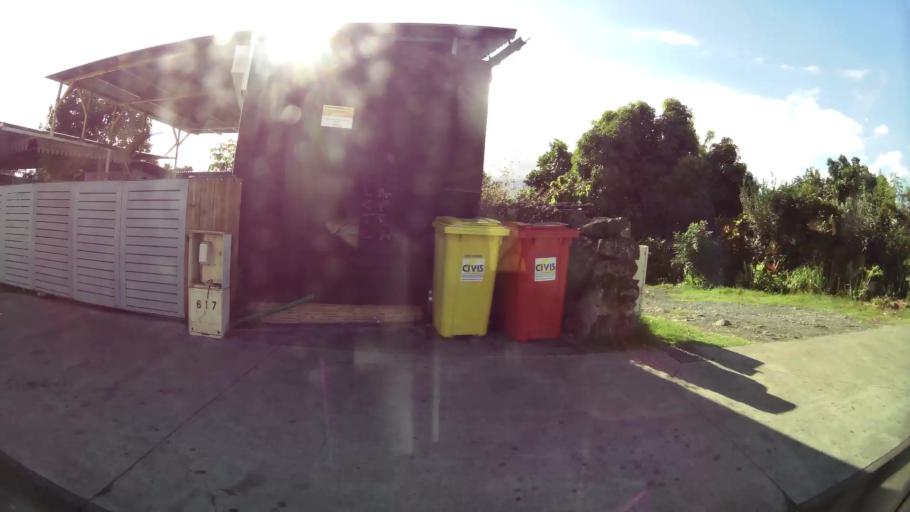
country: RE
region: Reunion
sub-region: Reunion
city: Saint-Louis
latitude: -21.2900
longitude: 55.4146
